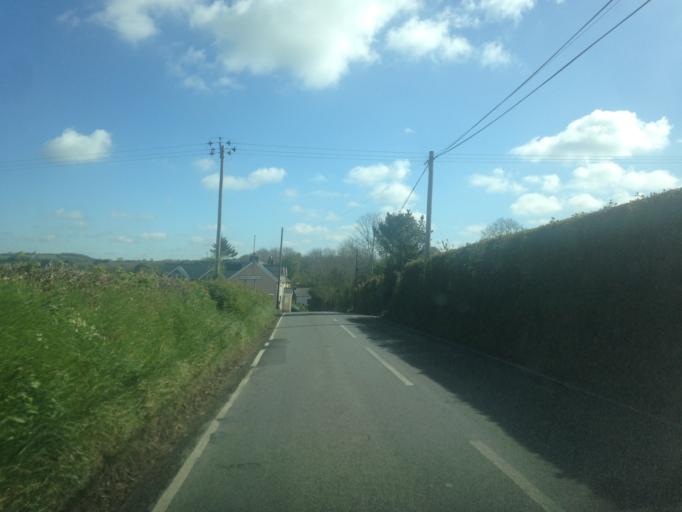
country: GB
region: Wales
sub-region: County of Ceredigion
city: Newcastle Emlyn
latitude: 52.0567
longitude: -4.4468
